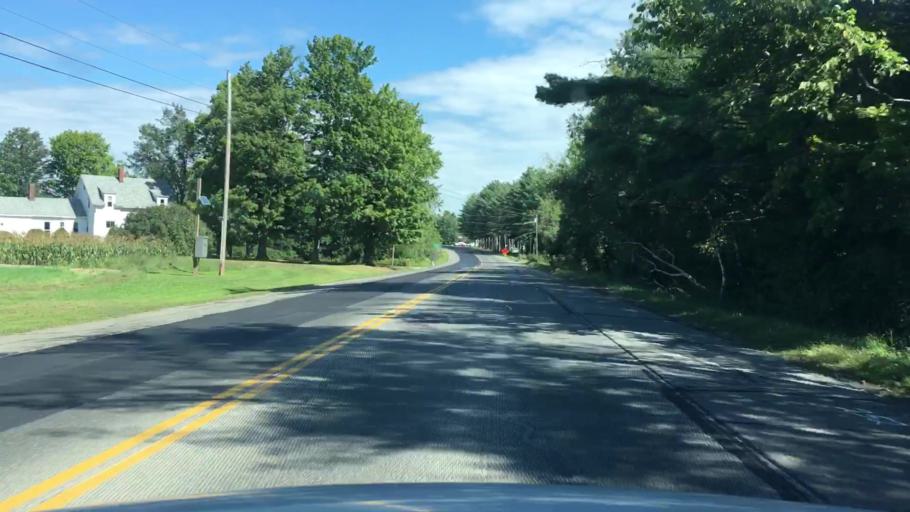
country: US
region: Maine
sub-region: Penobscot County
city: Corinna
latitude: 44.8996
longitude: -69.2671
